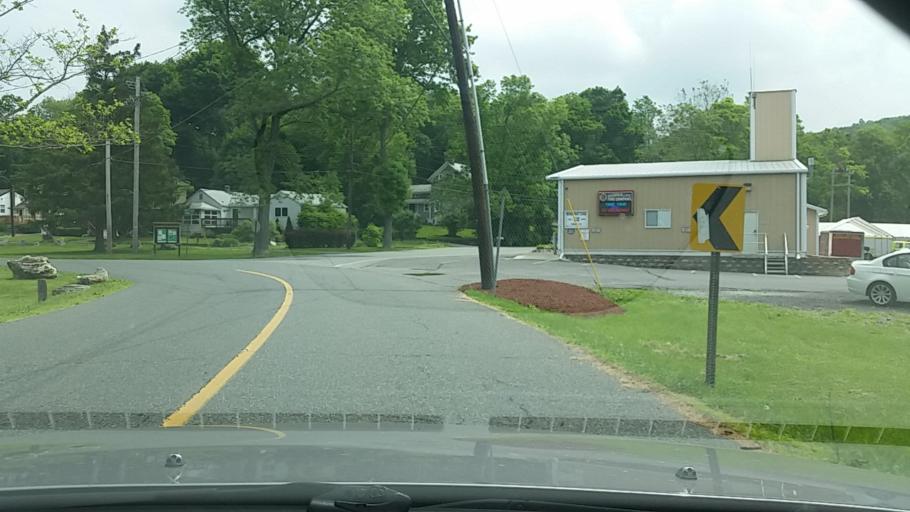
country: US
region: New Jersey
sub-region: Warren County
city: Oxford
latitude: 40.8530
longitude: -74.9849
